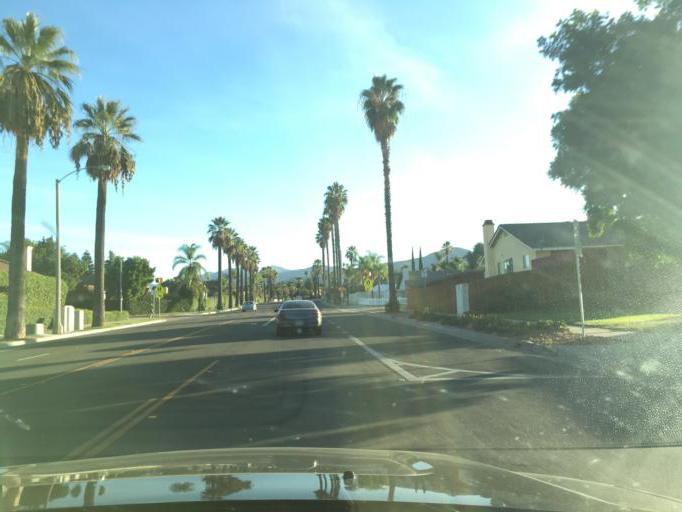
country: US
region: California
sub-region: Riverside County
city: Corona
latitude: 33.8559
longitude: -117.5504
